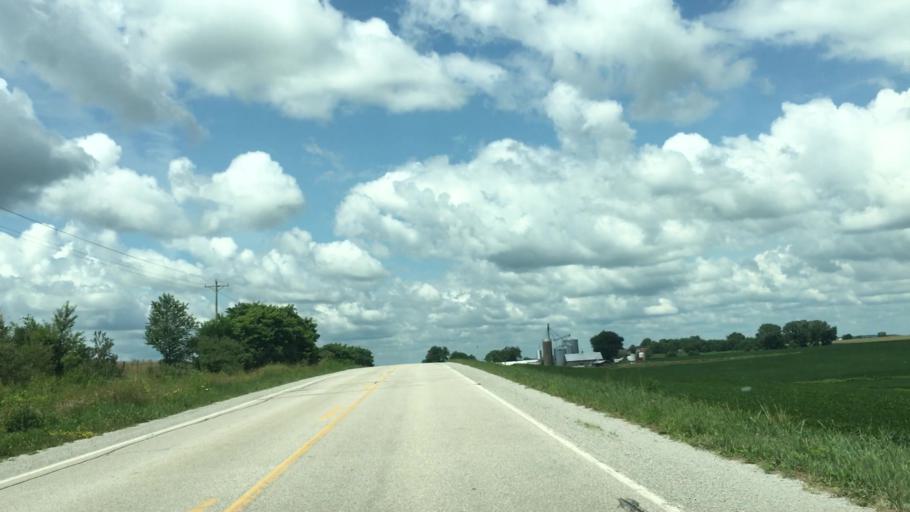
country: US
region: Iowa
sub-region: Johnson County
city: Solon
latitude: 41.8305
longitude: -91.4848
